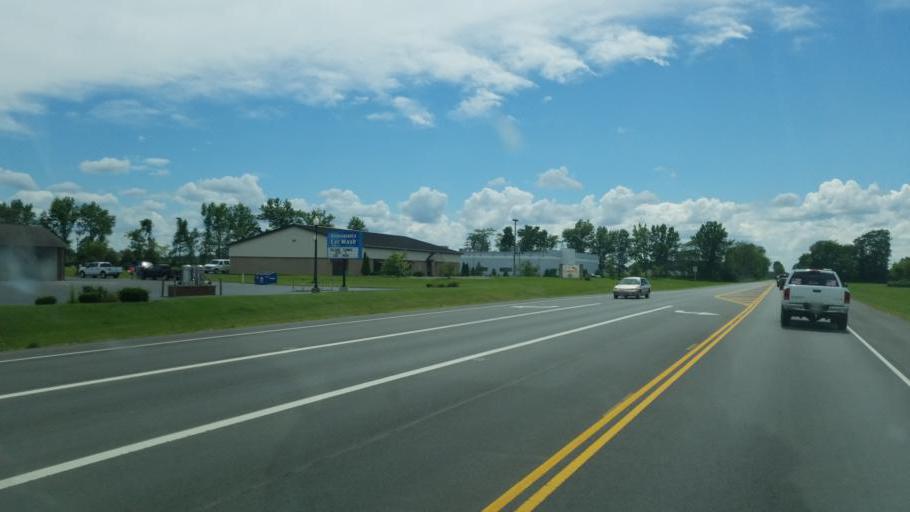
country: US
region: Ohio
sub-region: Delaware County
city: Sunbury
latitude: 40.2422
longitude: -82.8686
